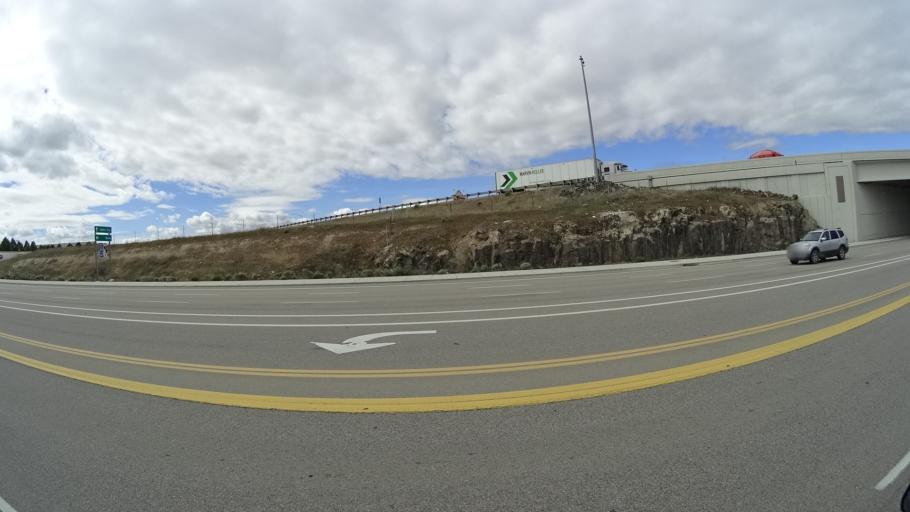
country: US
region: Idaho
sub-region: Ada County
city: Boise
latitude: 43.5420
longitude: -116.1600
